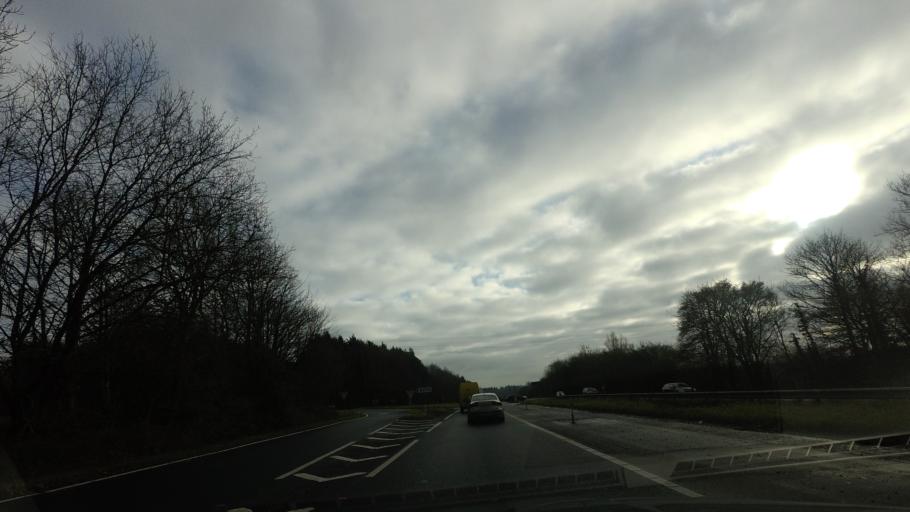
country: GB
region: England
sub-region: Kent
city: Hawkhurst
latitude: 51.0653
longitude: 0.4396
